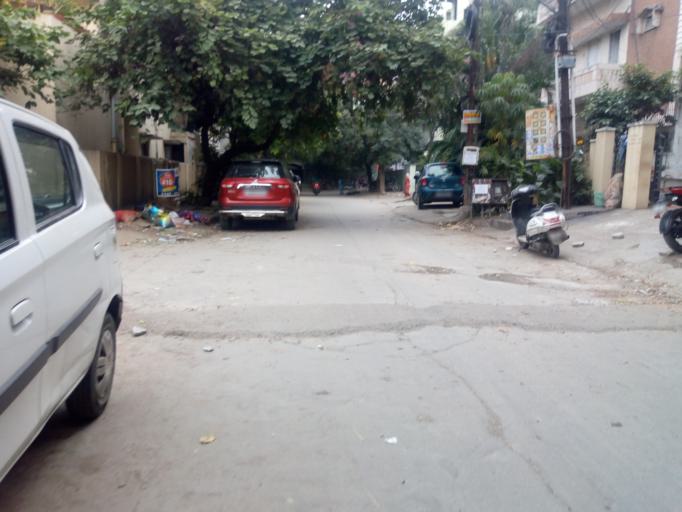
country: IN
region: Telangana
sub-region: Hyderabad
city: Hyderabad
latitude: 17.4347
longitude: 78.4423
